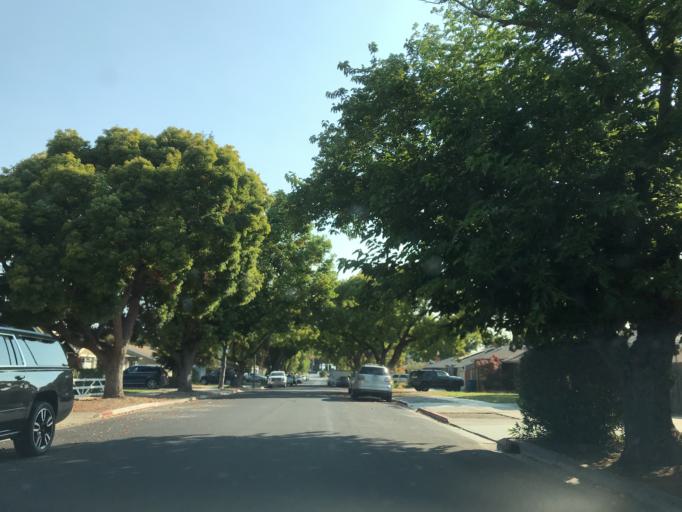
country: US
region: California
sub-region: San Mateo County
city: Redwood City
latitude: 37.4966
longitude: -122.2423
